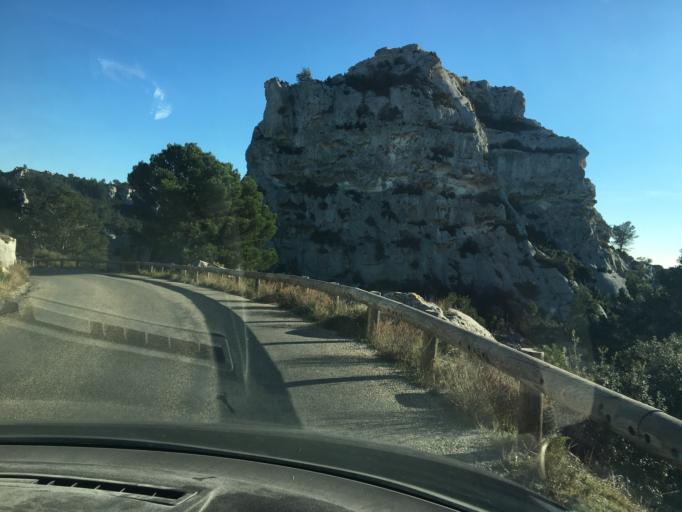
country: FR
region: Provence-Alpes-Cote d'Azur
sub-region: Departement des Bouches-du-Rhone
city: Maussane-les-Alpilles
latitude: 43.7519
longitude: 4.7914
